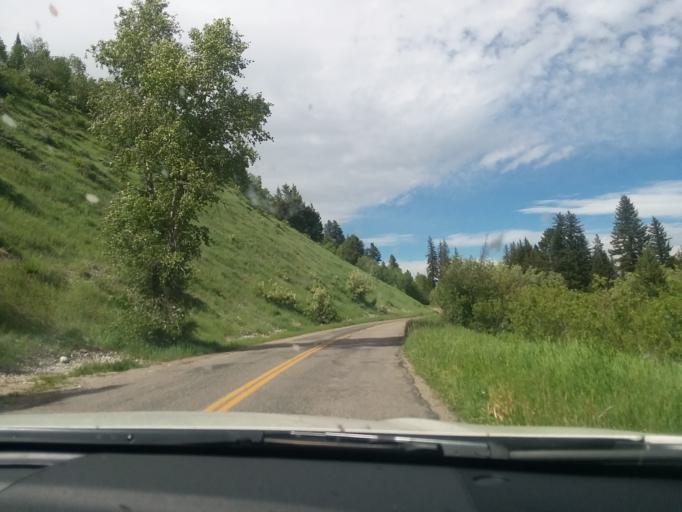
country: US
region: Wyoming
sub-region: Teton County
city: Moose Wilson Road
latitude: 43.5241
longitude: -110.8633
